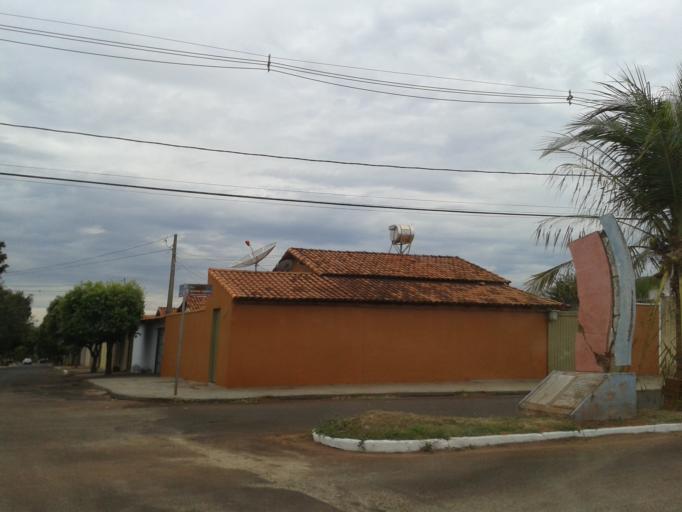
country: BR
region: Minas Gerais
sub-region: Santa Vitoria
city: Santa Vitoria
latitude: -18.8524
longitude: -50.1214
